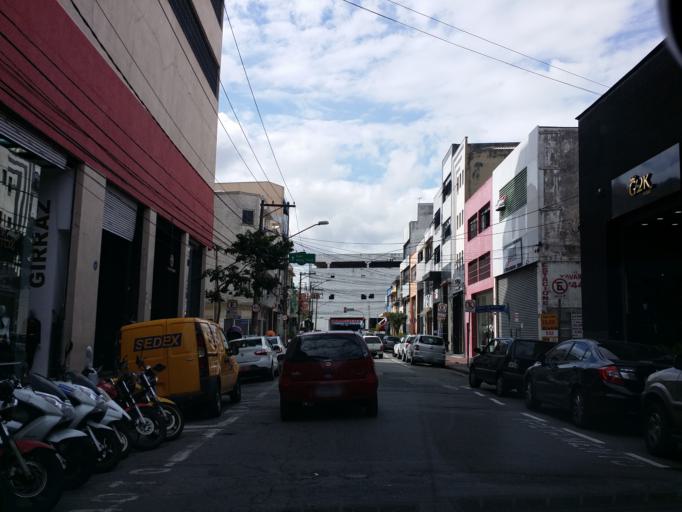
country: BR
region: Sao Paulo
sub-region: Sao Paulo
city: Sao Paulo
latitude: -23.5347
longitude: -46.6132
